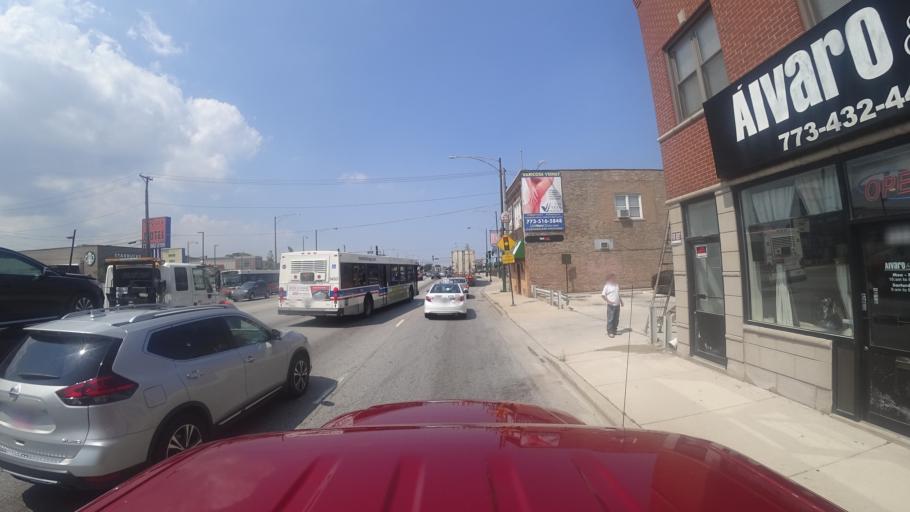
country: US
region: Illinois
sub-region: Cook County
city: Stickney
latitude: 41.7978
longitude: -87.7428
